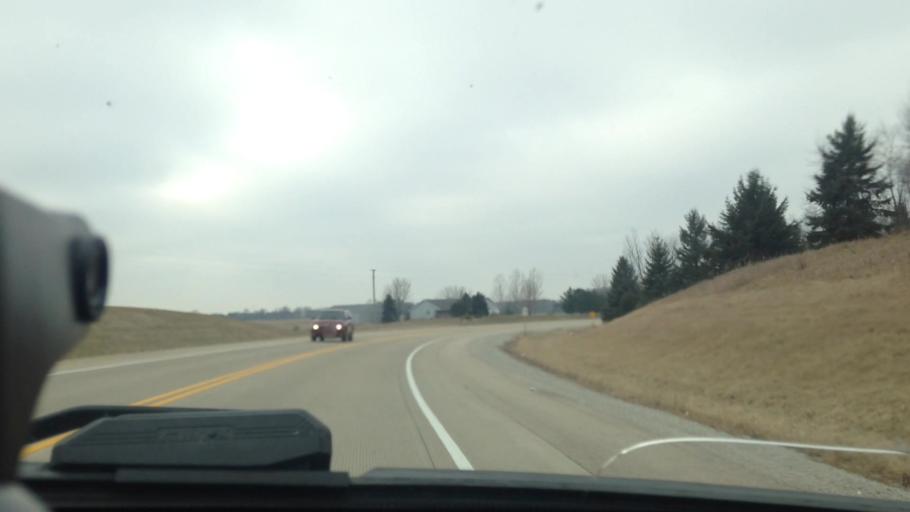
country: US
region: Wisconsin
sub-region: Dodge County
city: Beaver Dam
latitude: 43.4671
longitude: -88.7625
